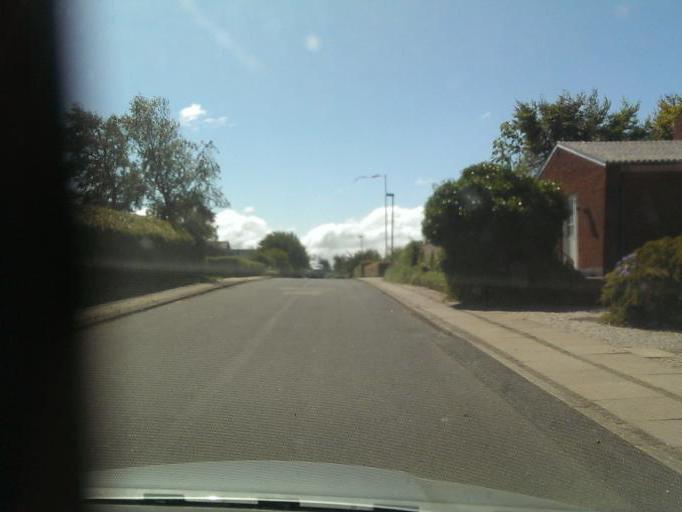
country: DK
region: North Denmark
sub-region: Jammerbugt Kommune
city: Pandrup
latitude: 57.3142
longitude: 9.7079
